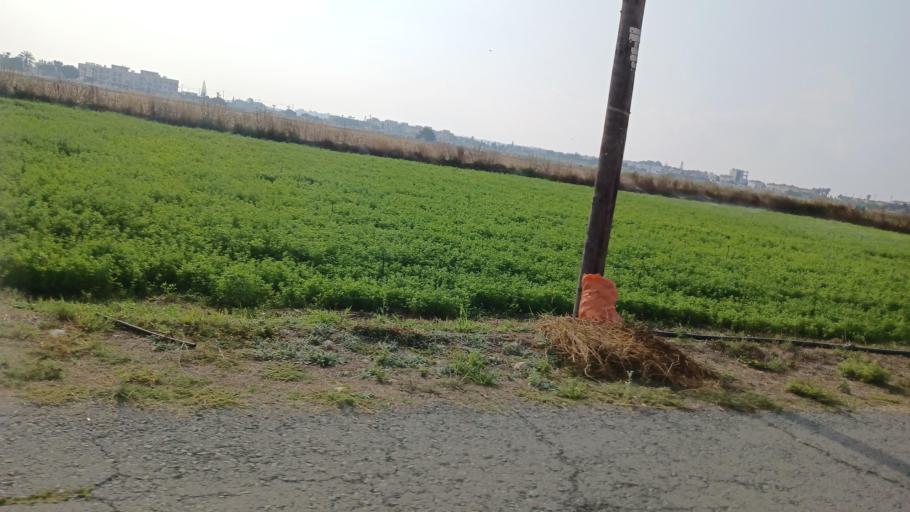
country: CY
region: Larnaka
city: Perivolia
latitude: 34.8253
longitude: 33.5781
